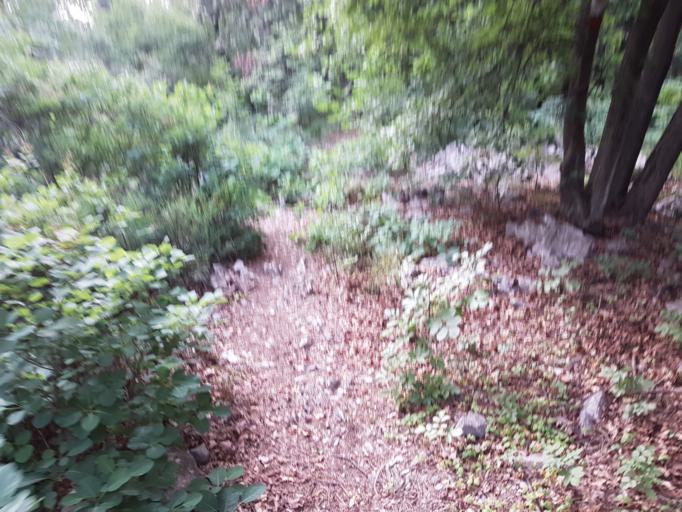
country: IT
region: Friuli Venezia Giulia
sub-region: Provincia di Trieste
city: Aurisina
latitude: 45.7465
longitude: 13.6660
